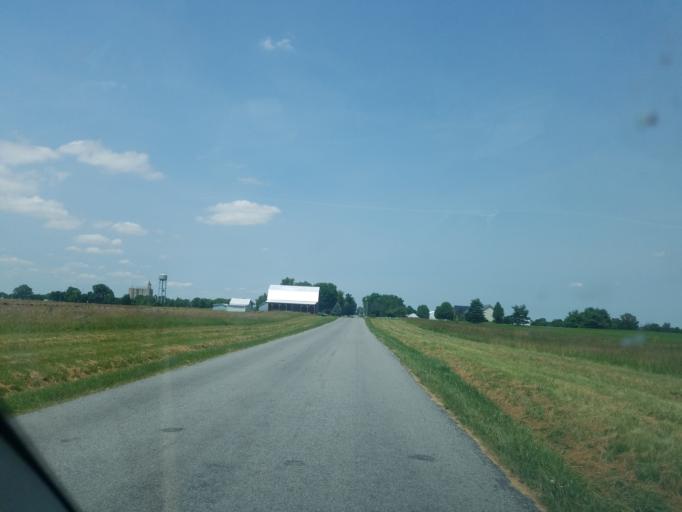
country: US
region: Ohio
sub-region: Wyandot County
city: Carey
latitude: 40.9665
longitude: -83.4768
